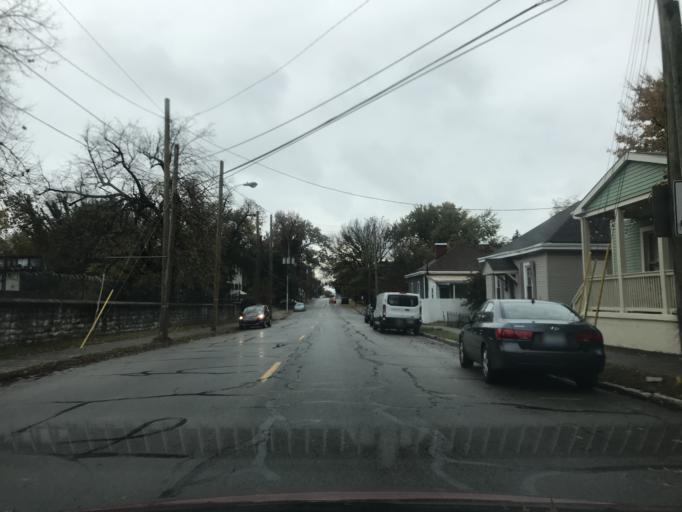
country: US
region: Kentucky
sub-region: Jefferson County
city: Audubon Park
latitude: 38.2363
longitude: -85.7211
